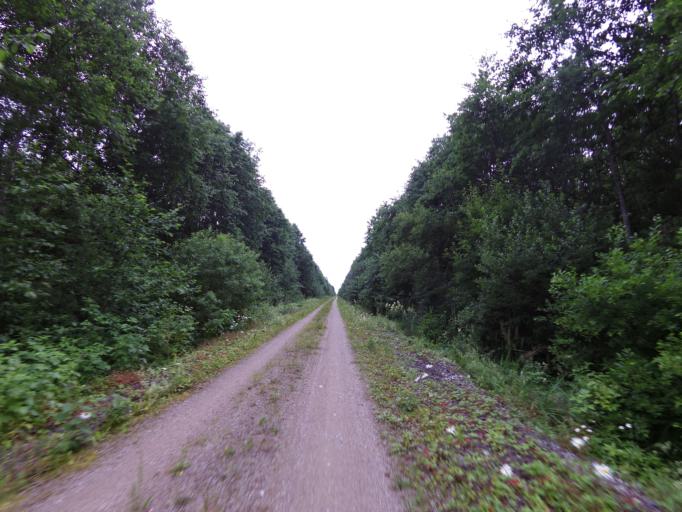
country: EE
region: Harju
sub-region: Nissi vald
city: Turba
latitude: 59.0216
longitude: 24.1012
